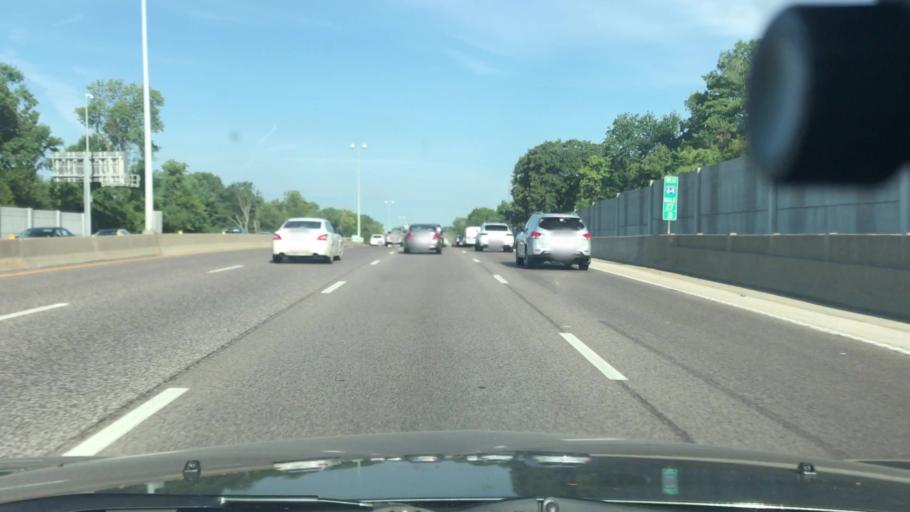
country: US
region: Missouri
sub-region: Saint Louis County
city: Frontenac
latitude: 38.6370
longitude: -90.4281
